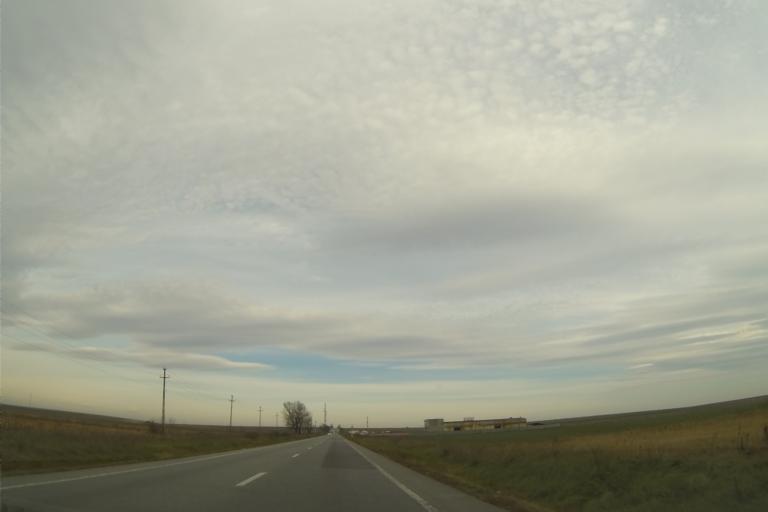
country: RO
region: Olt
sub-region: Comuna Valea Mare
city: Valea Mare
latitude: 44.4681
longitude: 24.4172
